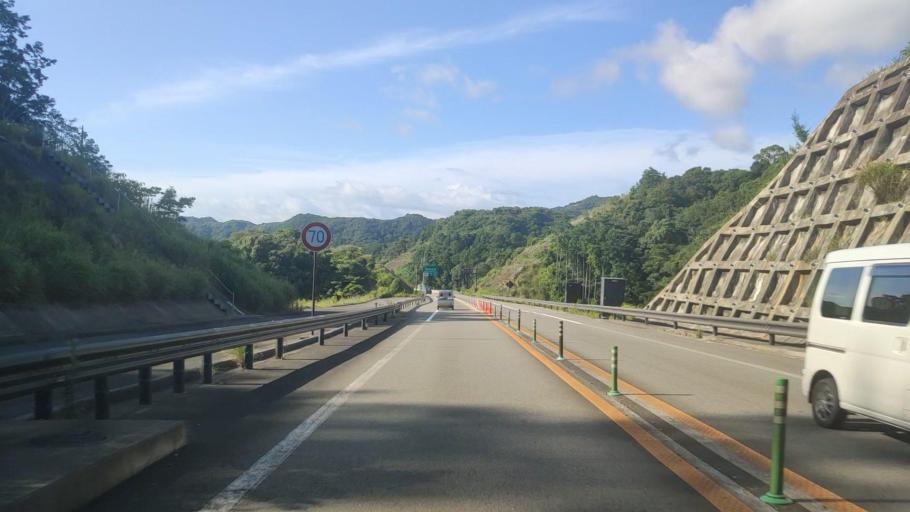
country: JP
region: Wakayama
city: Tanabe
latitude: 33.6439
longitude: 135.4099
